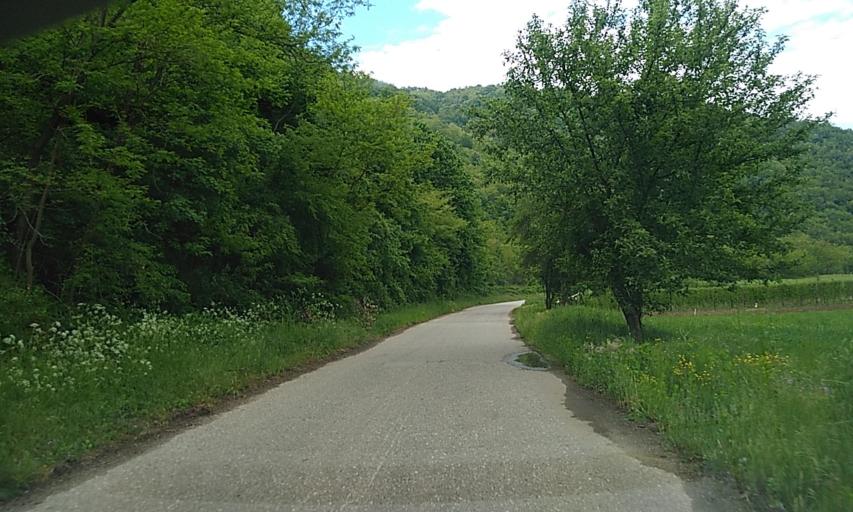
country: RS
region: Central Serbia
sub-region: Pcinjski Okrug
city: Vladicin Han
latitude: 42.7505
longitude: 22.0612
